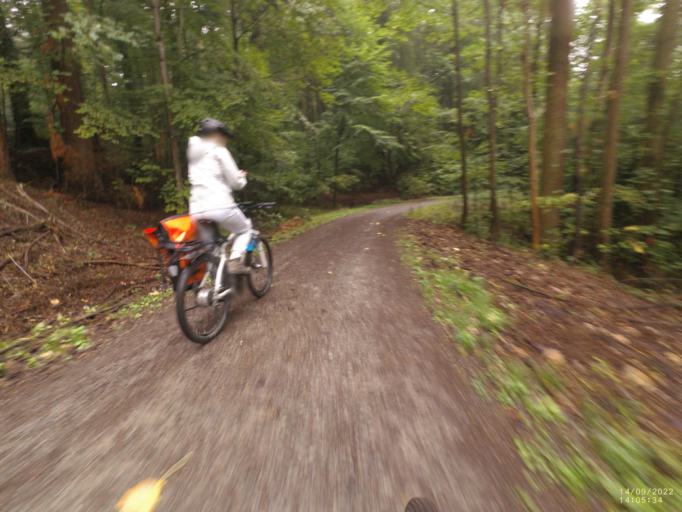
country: DE
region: Bavaria
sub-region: Regierungsbezirk Unterfranken
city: Johannesberg
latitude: 50.0188
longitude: 9.1456
